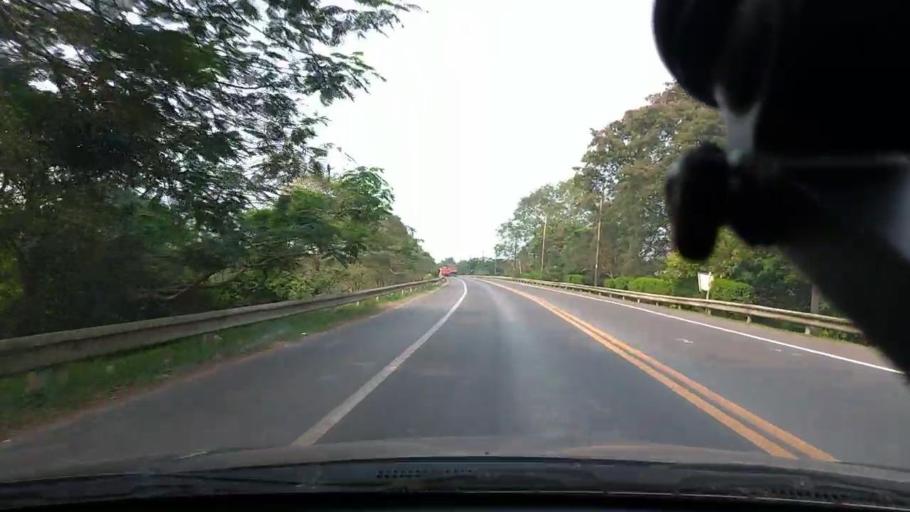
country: ID
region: Banten
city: Serang
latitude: -6.0910
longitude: 106.1394
